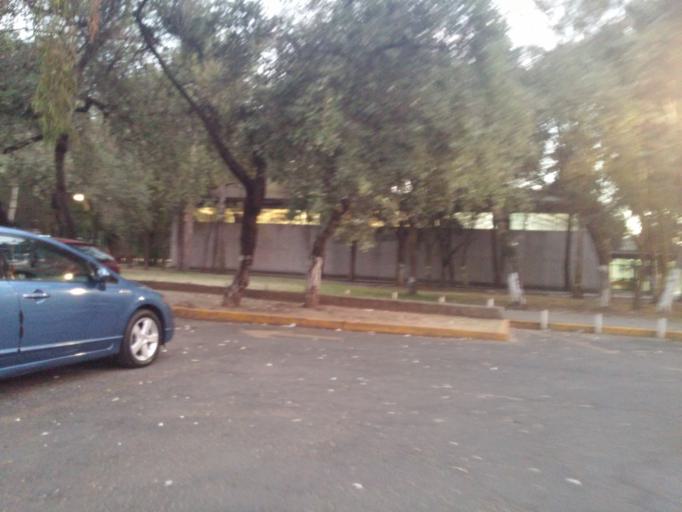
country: MX
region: Mexico
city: Colonia Lindavista
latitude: 19.4984
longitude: -99.1391
